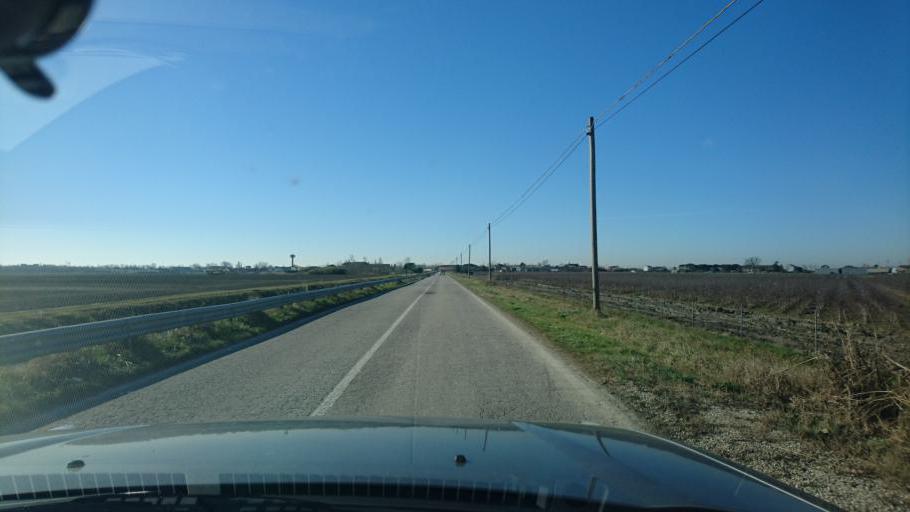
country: IT
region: Emilia-Romagna
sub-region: Provincia di Ferrara
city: Mesola
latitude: 44.9423
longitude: 12.2322
